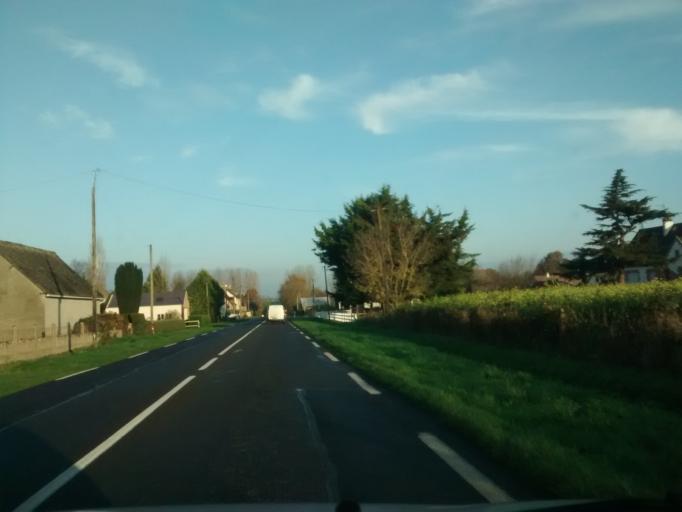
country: FR
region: Lower Normandy
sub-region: Departement de la Manche
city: Pontorson
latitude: 48.5241
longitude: -1.4837
